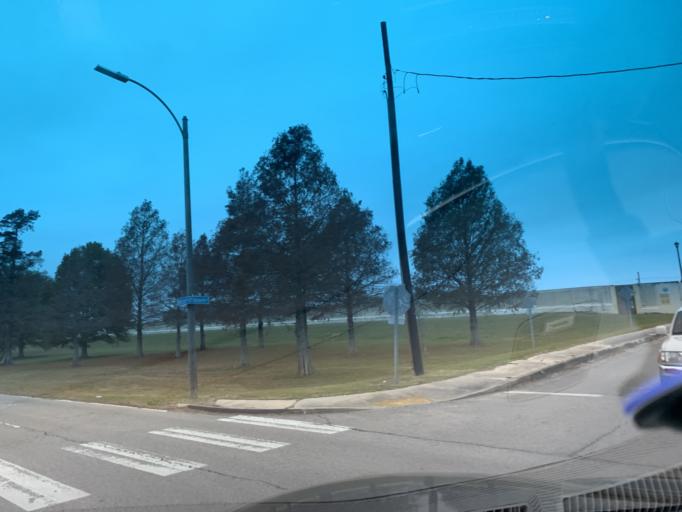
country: US
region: Louisiana
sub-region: Jefferson Parish
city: Metairie
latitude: 30.0114
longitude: -90.0983
